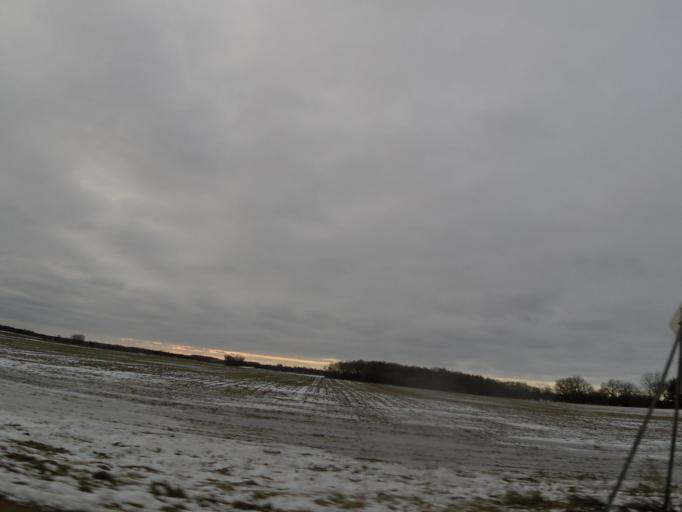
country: US
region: Minnesota
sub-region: Scott County
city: Jordan
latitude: 44.7121
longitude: -93.6487
